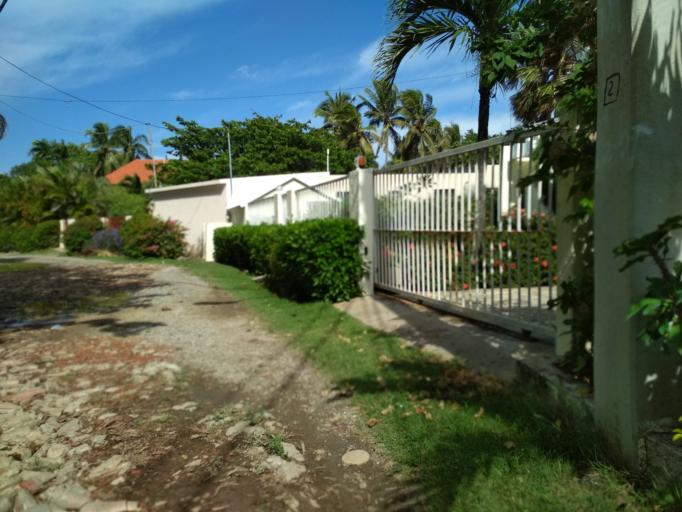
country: DO
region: Puerto Plata
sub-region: Puerto Plata
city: Puerto Plata
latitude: 19.8074
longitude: -70.7052
